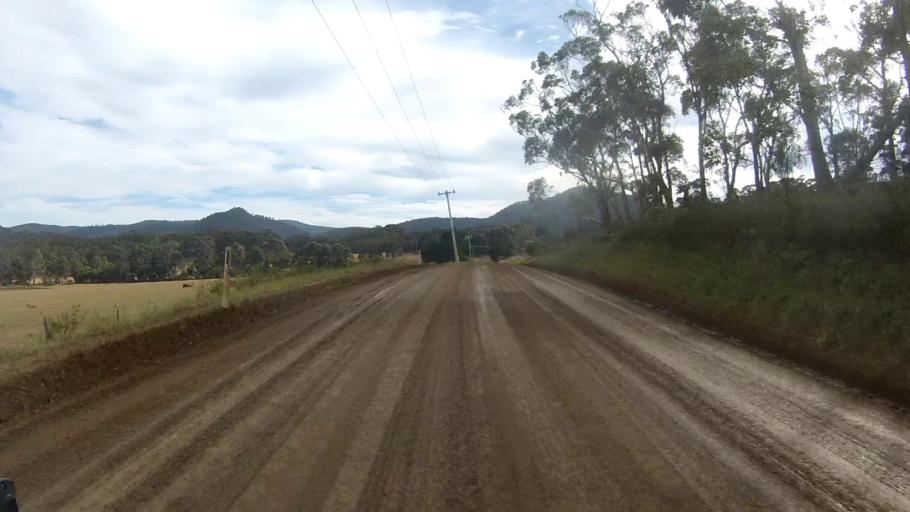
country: AU
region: Tasmania
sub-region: Sorell
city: Sorell
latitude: -42.7834
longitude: 147.8082
